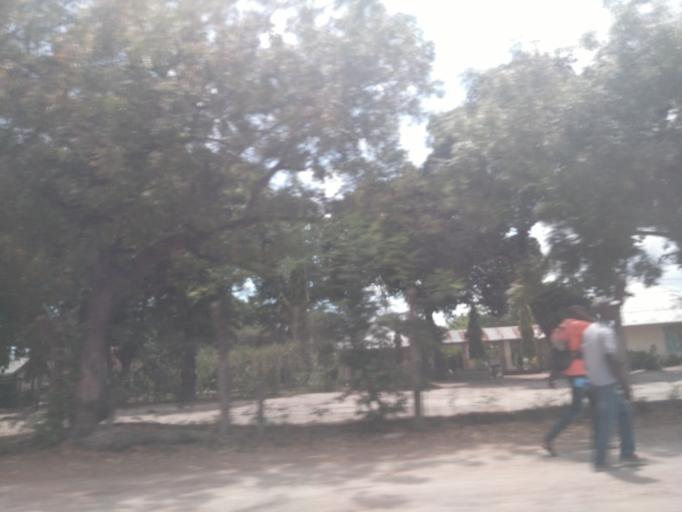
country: TZ
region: Dar es Salaam
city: Dar es Salaam
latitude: -6.8490
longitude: 39.2714
